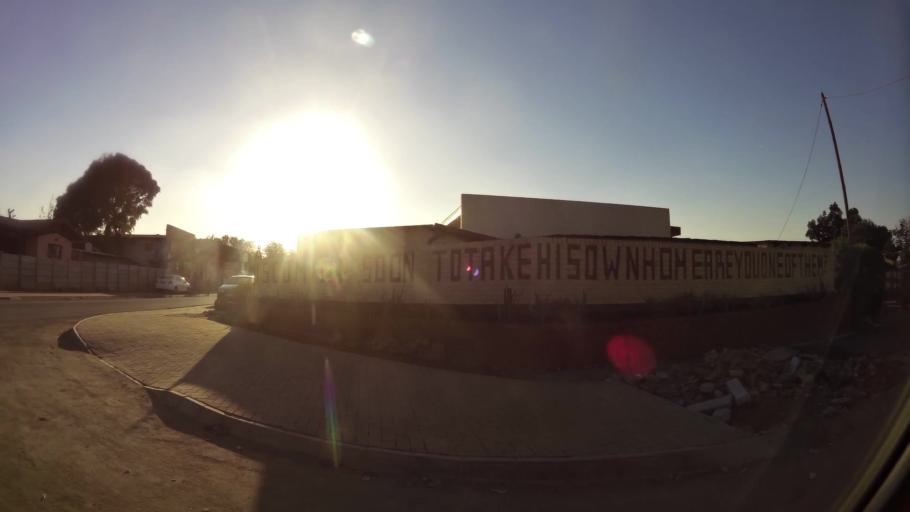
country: ZA
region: North-West
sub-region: Bojanala Platinum District Municipality
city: Rustenburg
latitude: -25.6417
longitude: 27.2176
